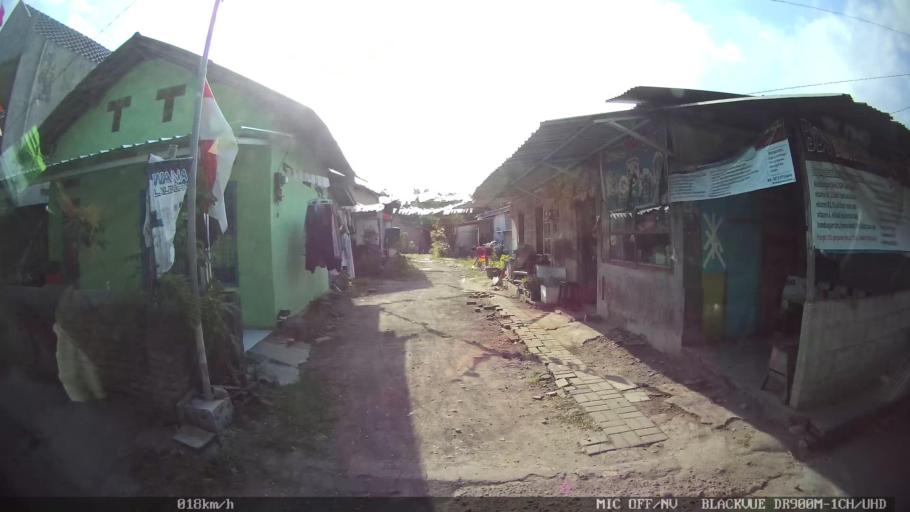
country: ID
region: Daerah Istimewa Yogyakarta
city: Yogyakarta
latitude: -7.7992
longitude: 110.3486
